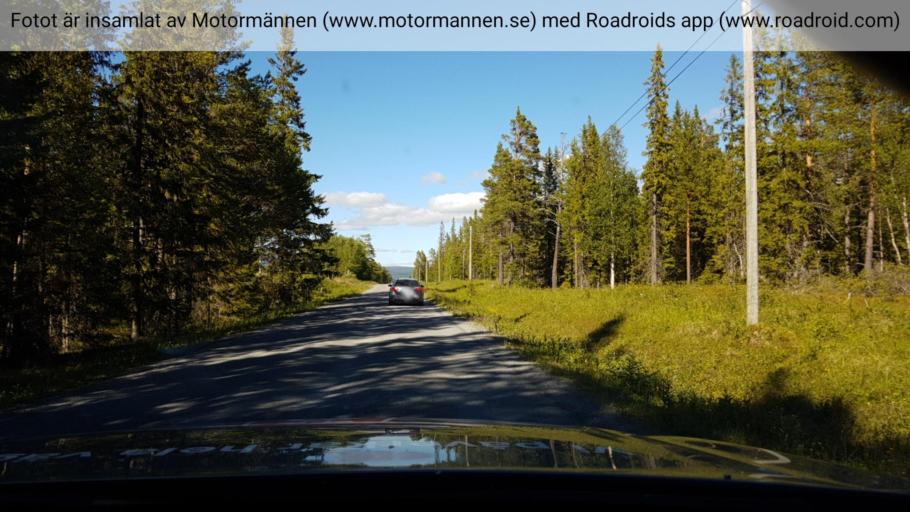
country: SE
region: Jaemtland
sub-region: Are Kommun
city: Are
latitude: 63.1642
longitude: 13.0744
